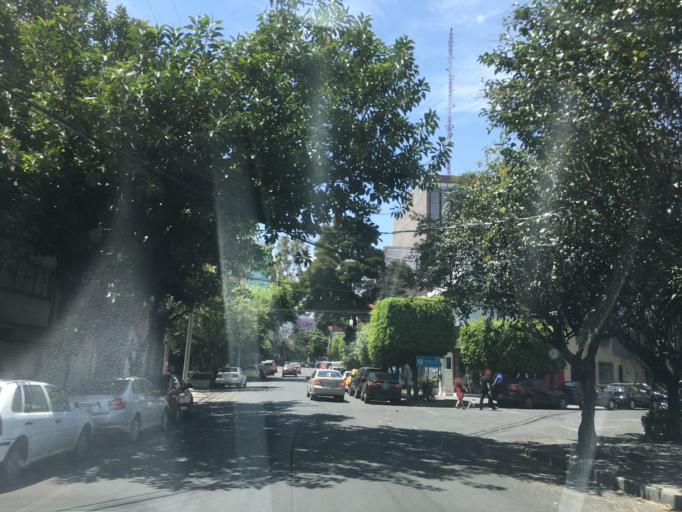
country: MX
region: Mexico City
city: Colonia del Valle
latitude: 19.3959
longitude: -99.1707
